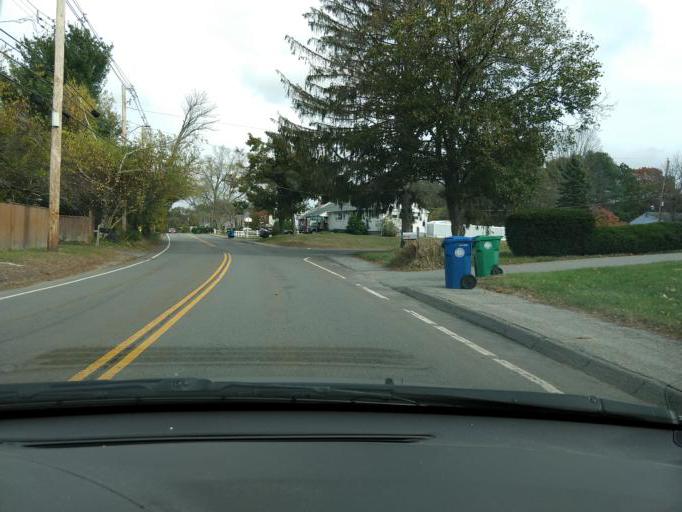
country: US
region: Massachusetts
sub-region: Middlesex County
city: Pinehurst
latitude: 42.5169
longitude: -71.2249
